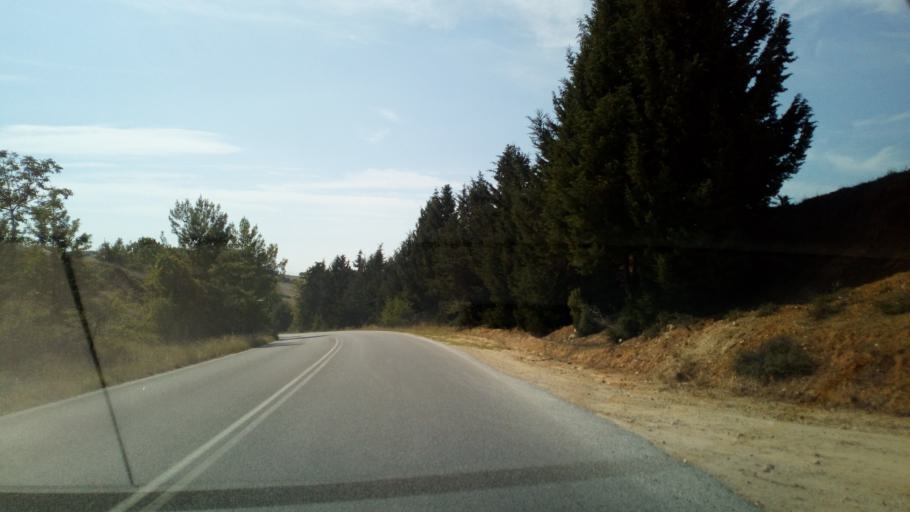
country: GR
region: Central Macedonia
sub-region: Nomos Chalkidikis
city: Arnaia
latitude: 40.5041
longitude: 23.4826
